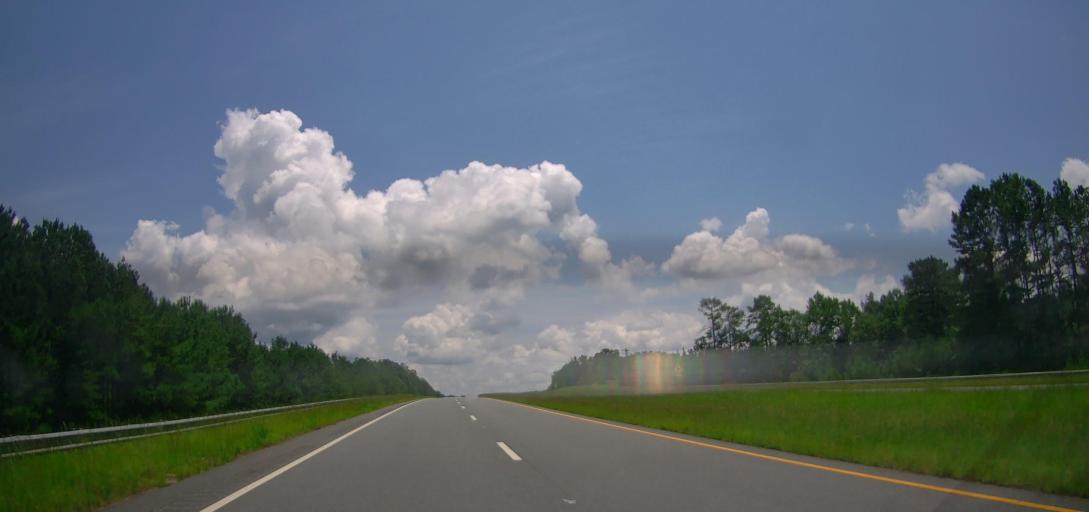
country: US
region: Georgia
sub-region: Upson County
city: Thomaston
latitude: 32.7920
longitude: -84.2556
